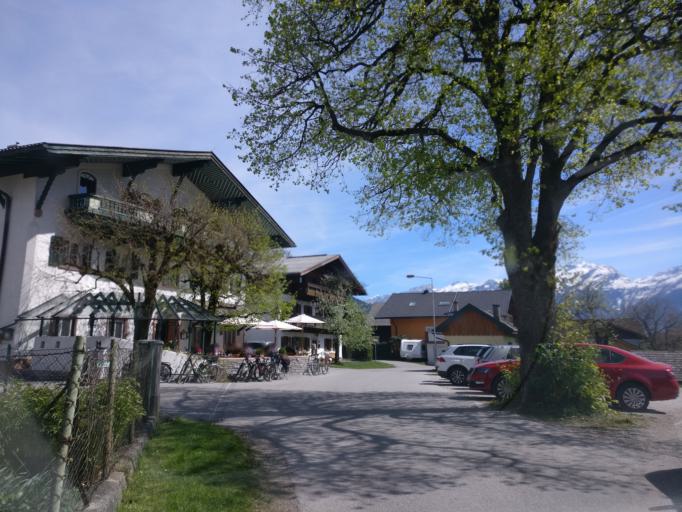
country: AT
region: Salzburg
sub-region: Politischer Bezirk Hallein
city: Kuchl
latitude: 47.6374
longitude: 13.1482
